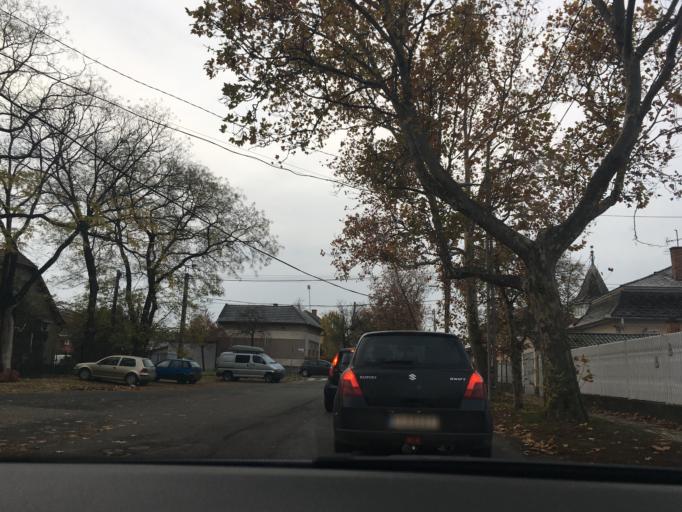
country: HU
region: Hajdu-Bihar
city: Debrecen
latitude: 47.5353
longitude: 21.6486
